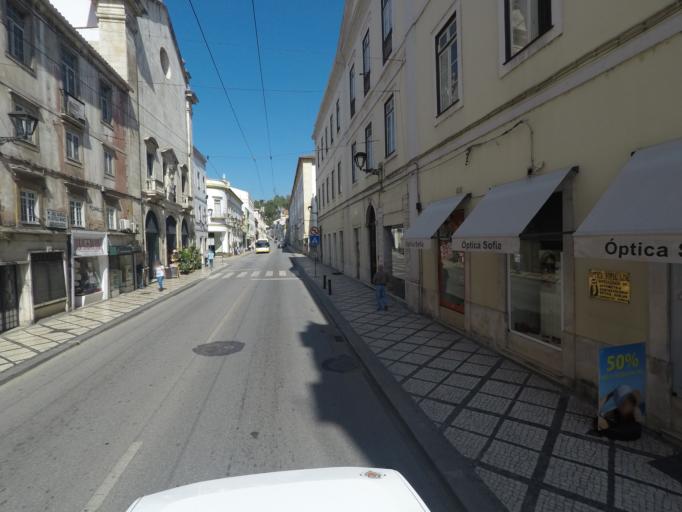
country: PT
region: Coimbra
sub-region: Coimbra
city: Coimbra
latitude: 40.2129
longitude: -8.4306
